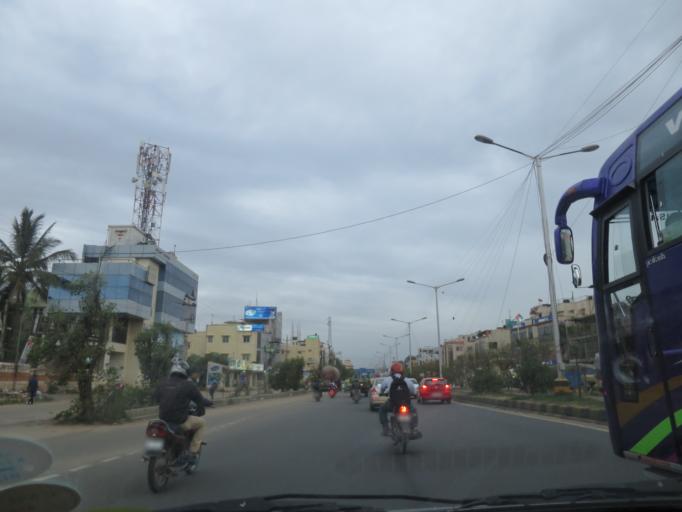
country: IN
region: Karnataka
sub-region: Bangalore Urban
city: Bangalore
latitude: 12.9634
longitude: 77.7019
